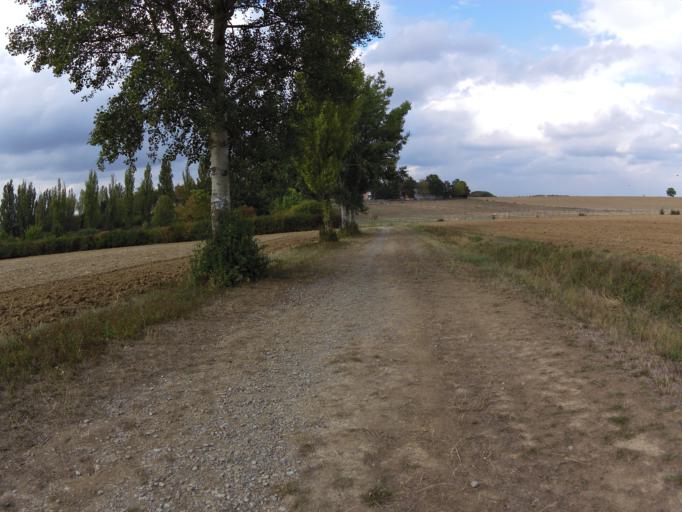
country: DE
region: Bavaria
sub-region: Regierungsbezirk Unterfranken
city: Kist
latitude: 49.7572
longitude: 9.8470
